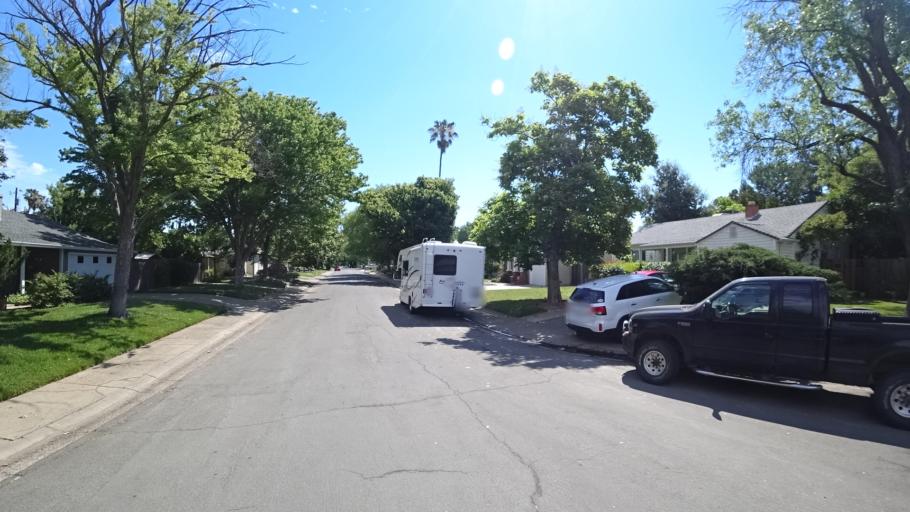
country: US
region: California
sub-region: Sacramento County
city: Arden-Arcade
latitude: 38.5687
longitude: -121.4315
